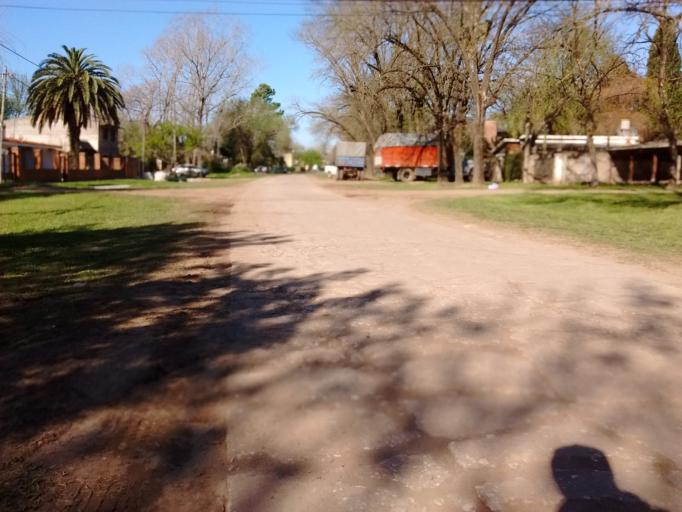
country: AR
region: Santa Fe
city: Funes
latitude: -32.9188
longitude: -60.8508
